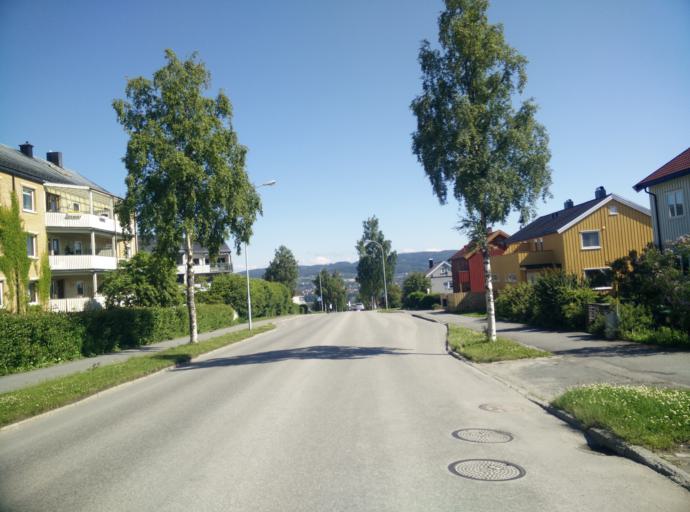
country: NO
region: Sor-Trondelag
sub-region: Trondheim
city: Trondheim
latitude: 63.4160
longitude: 10.3612
